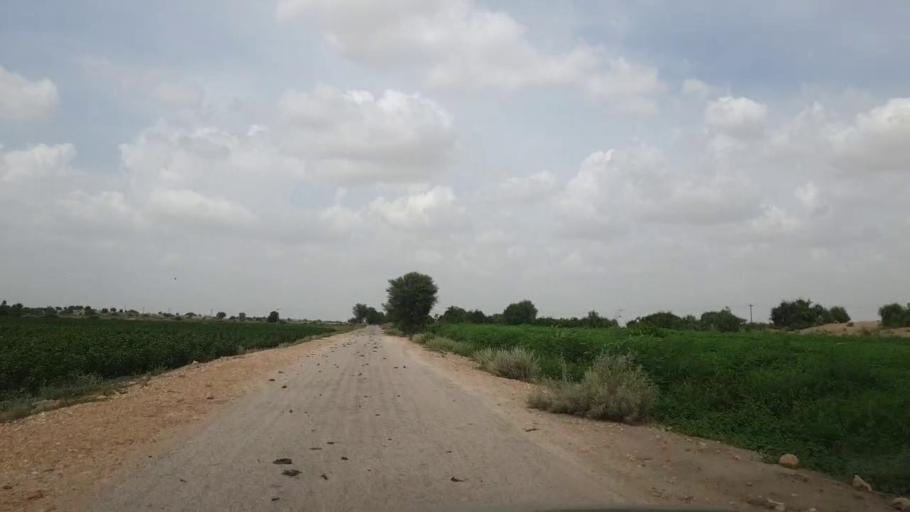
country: PK
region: Sindh
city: Kot Diji
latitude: 27.2225
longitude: 69.0848
